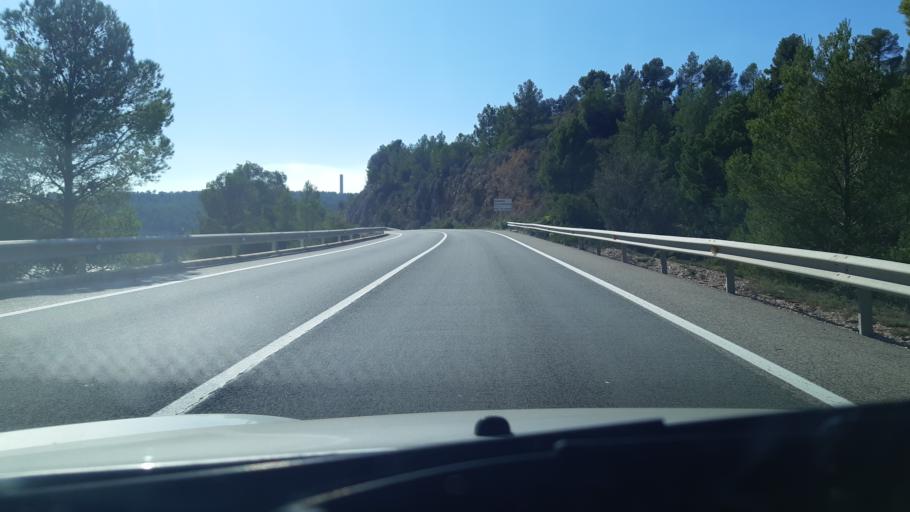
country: ES
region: Catalonia
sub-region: Provincia de Tarragona
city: Tivenys
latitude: 40.9380
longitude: 0.4879
